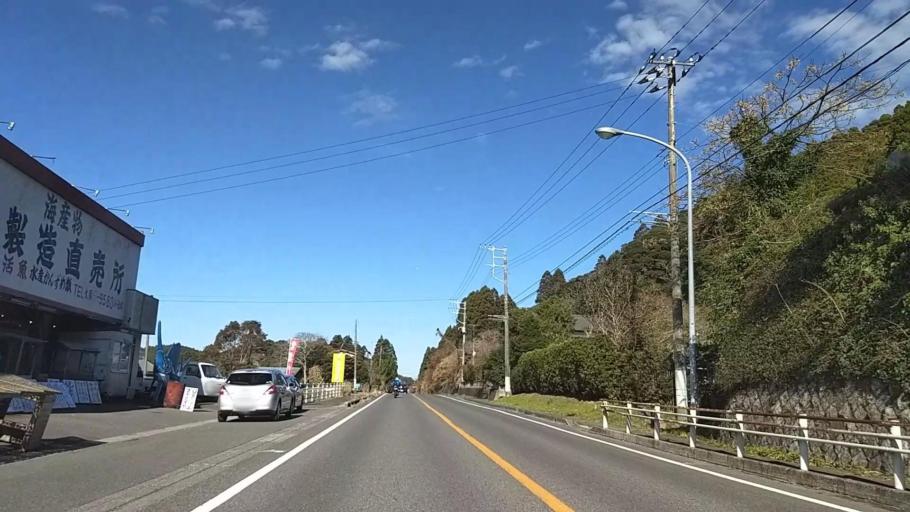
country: JP
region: Chiba
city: Ohara
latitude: 35.2074
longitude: 140.3747
